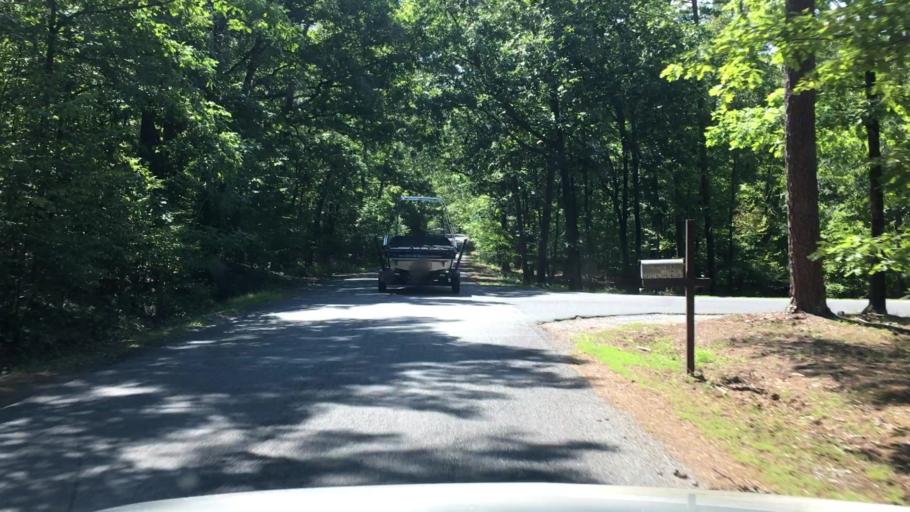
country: US
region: Arkansas
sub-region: Garland County
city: Piney
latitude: 34.5420
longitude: -93.3542
